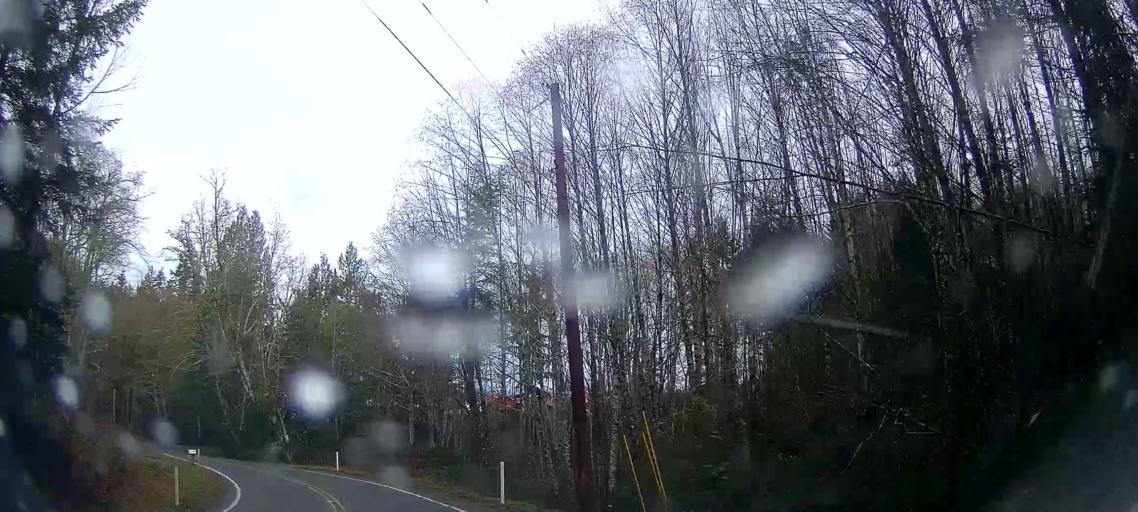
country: US
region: Washington
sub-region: Skagit County
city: Clear Lake
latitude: 48.4786
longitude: -122.1376
